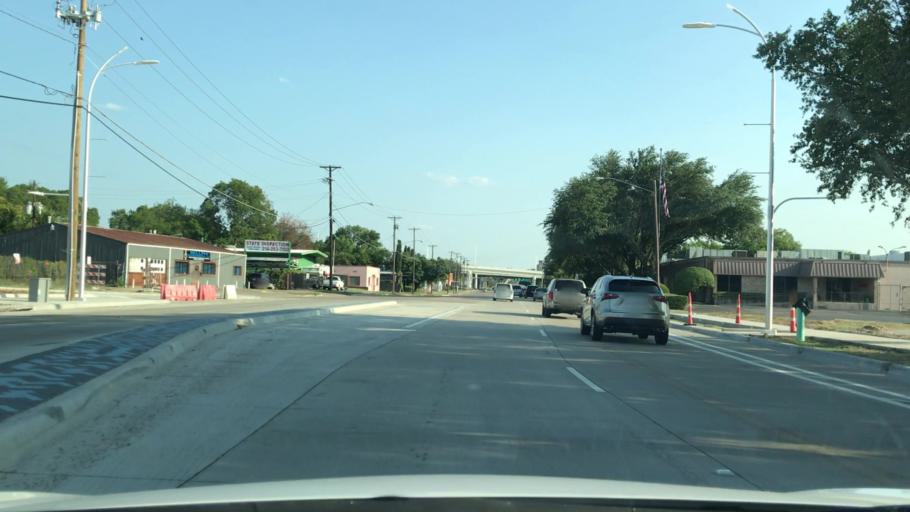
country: US
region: Texas
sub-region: Dallas County
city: Dallas
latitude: 32.7735
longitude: -96.8229
